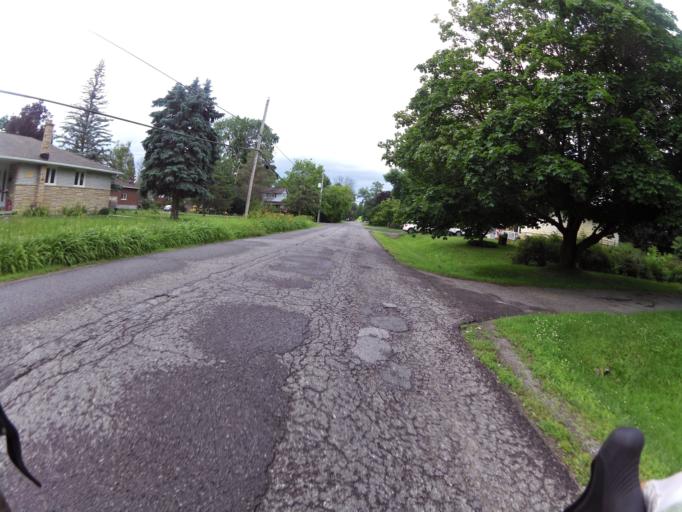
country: CA
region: Ontario
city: Bells Corners
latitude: 45.1916
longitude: -75.8392
